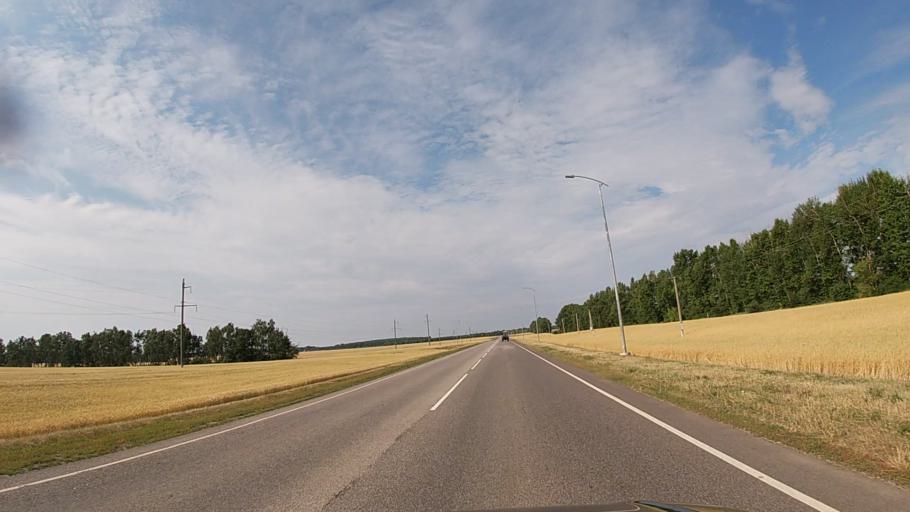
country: RU
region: Belgorod
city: Proletarskiy
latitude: 50.8146
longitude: 35.7508
